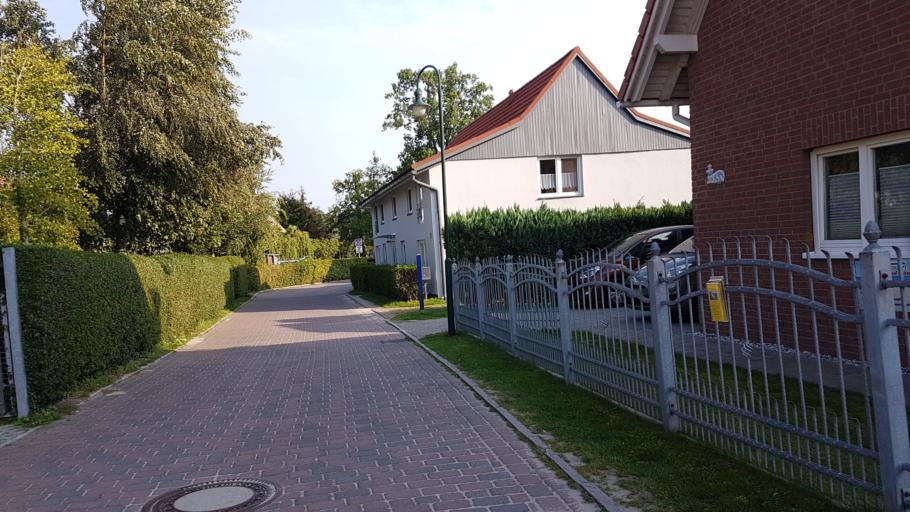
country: DE
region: Mecklenburg-Vorpommern
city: Glowe
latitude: 54.5707
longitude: 13.4703
